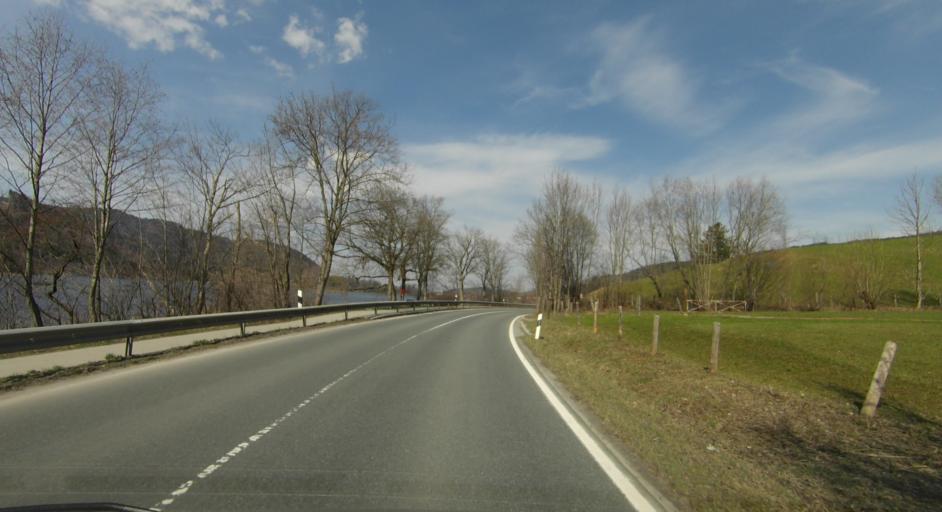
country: DE
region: Bavaria
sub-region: Upper Bavaria
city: Schliersee
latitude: 47.7199
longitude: 11.8694
